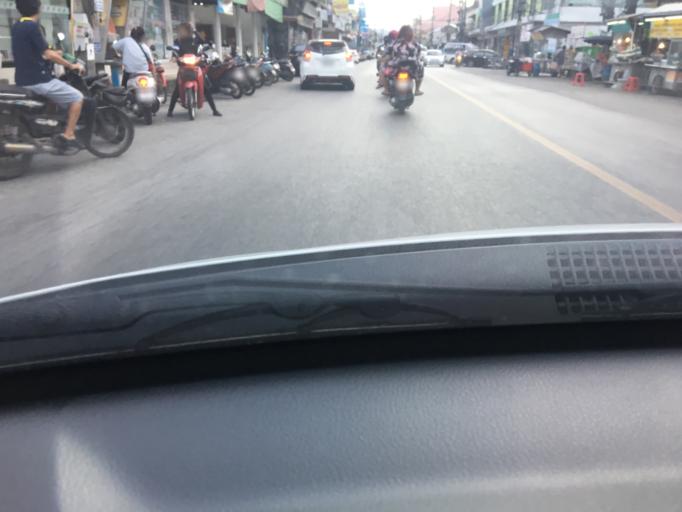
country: TH
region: Phuket
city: Ban Talat Yai
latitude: 7.8775
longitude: 98.3954
